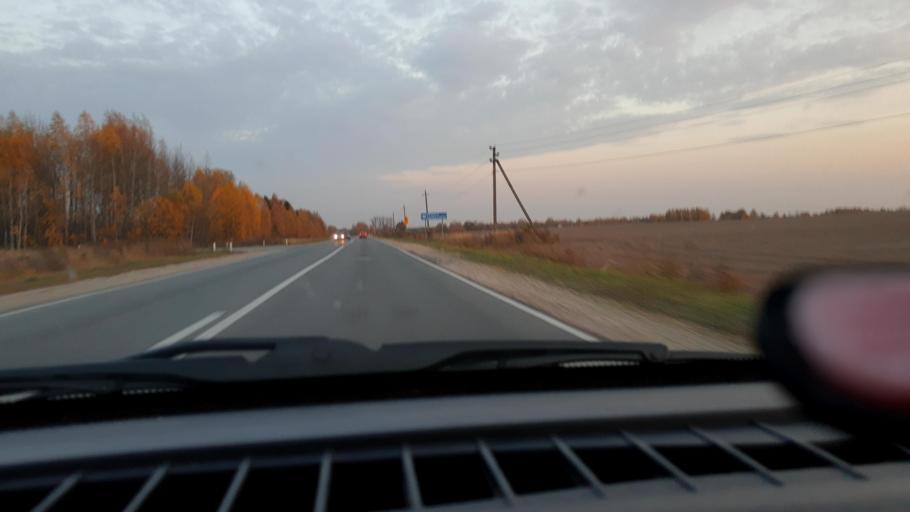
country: RU
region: Nizjnij Novgorod
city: Gorodets
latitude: 56.6226
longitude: 43.5516
